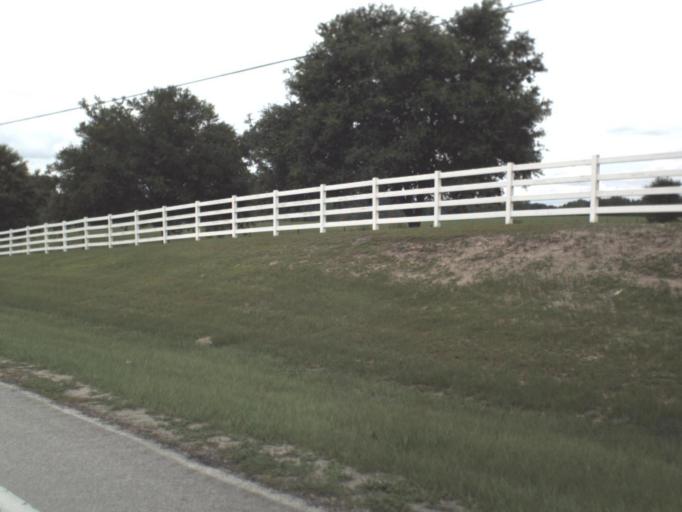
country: US
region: Florida
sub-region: Alachua County
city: Newberry
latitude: 29.6804
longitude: -82.6070
